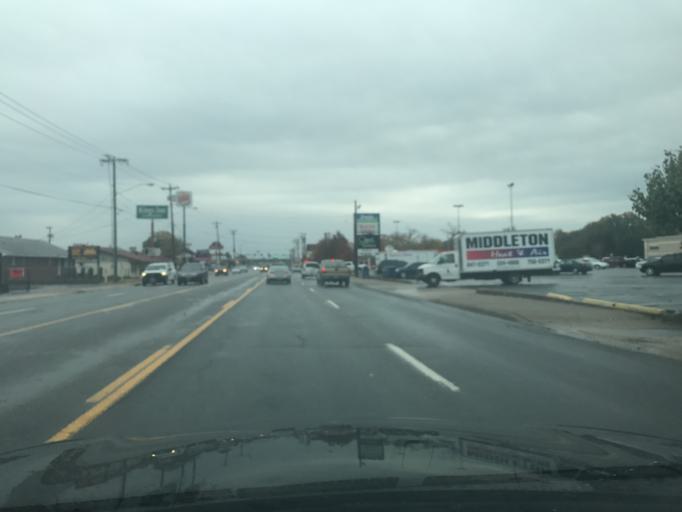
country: US
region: Arkansas
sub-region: Faulkner County
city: Conway
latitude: 35.0916
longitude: -92.4299
